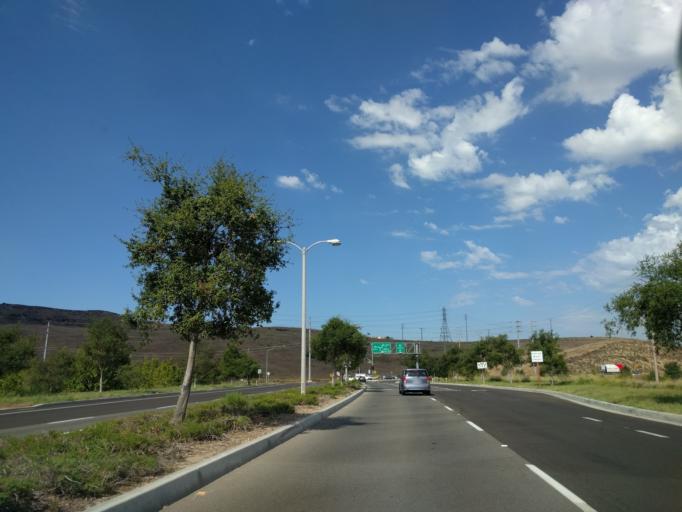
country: US
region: California
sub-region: Orange County
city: Laguna Woods
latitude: 33.6378
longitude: -117.7583
